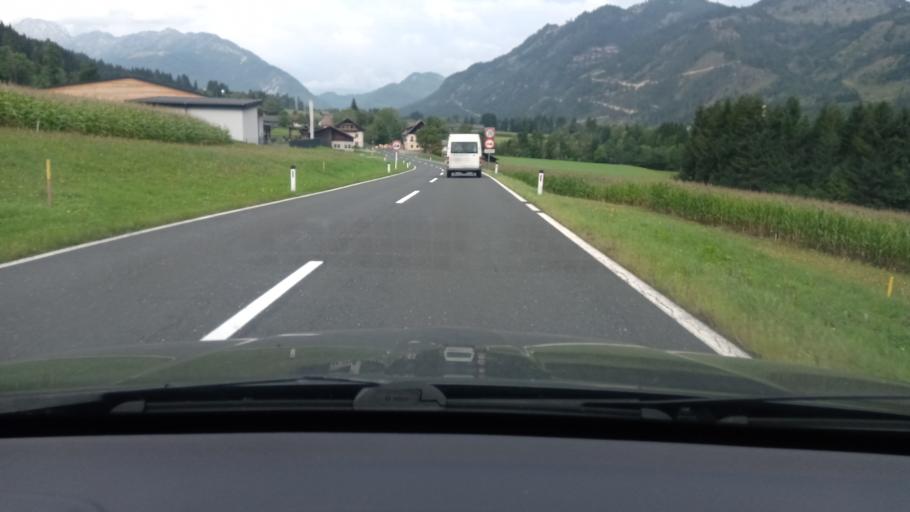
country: AT
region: Carinthia
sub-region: Politischer Bezirk Hermagor
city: Hermagor
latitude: 46.6586
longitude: 13.3157
